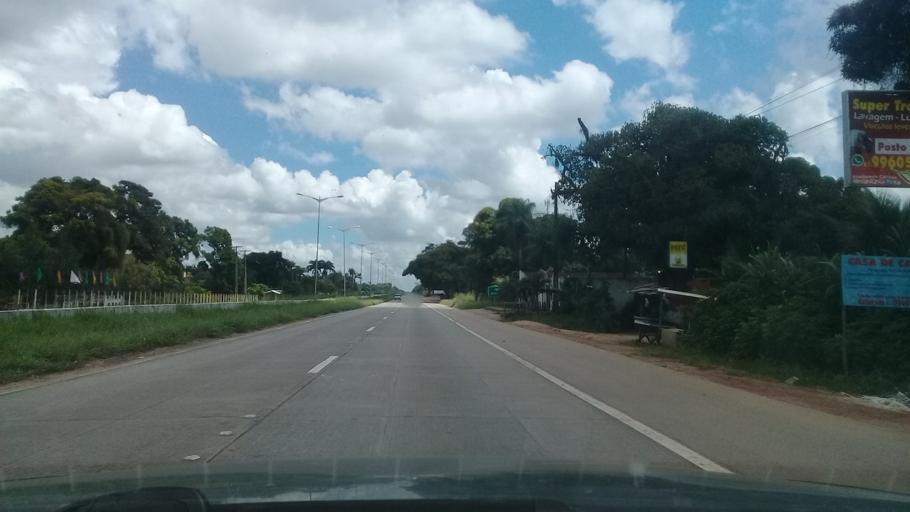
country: BR
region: Pernambuco
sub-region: Sao Lourenco Da Mata
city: Sao Lourenco da Mata
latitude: -7.9314
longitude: -35.1375
